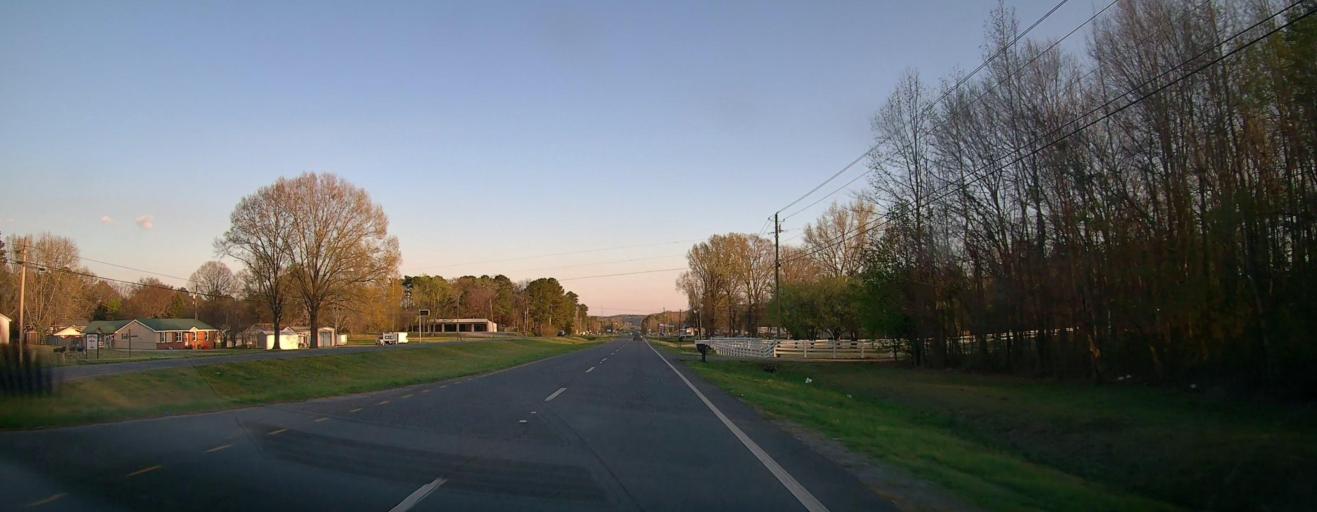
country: US
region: Alabama
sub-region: Talladega County
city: Childersburg
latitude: 33.2439
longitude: -86.3361
